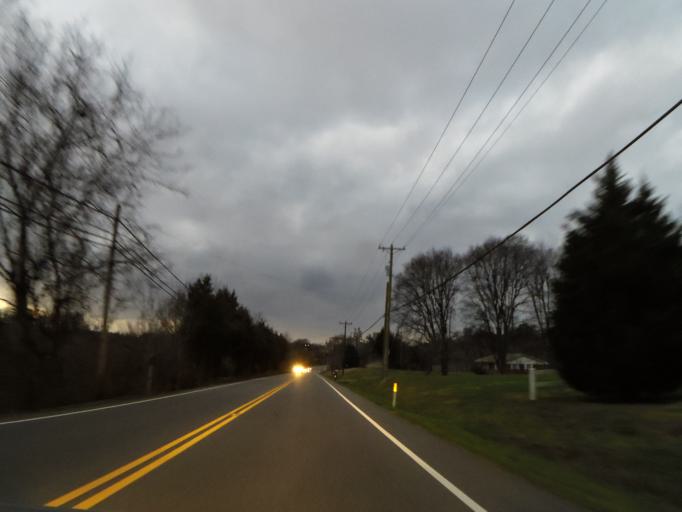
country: US
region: Tennessee
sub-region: Blount County
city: Eagleton Village
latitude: 35.8558
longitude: -83.9445
